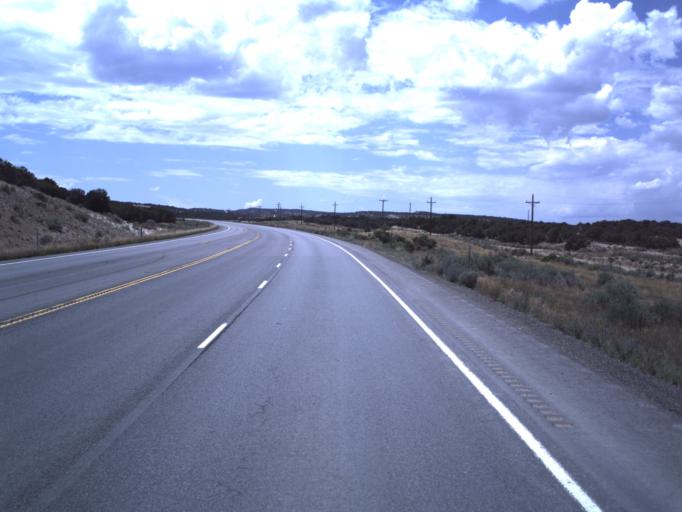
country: US
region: Utah
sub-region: Duchesne County
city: Duchesne
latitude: 40.1787
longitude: -110.5276
